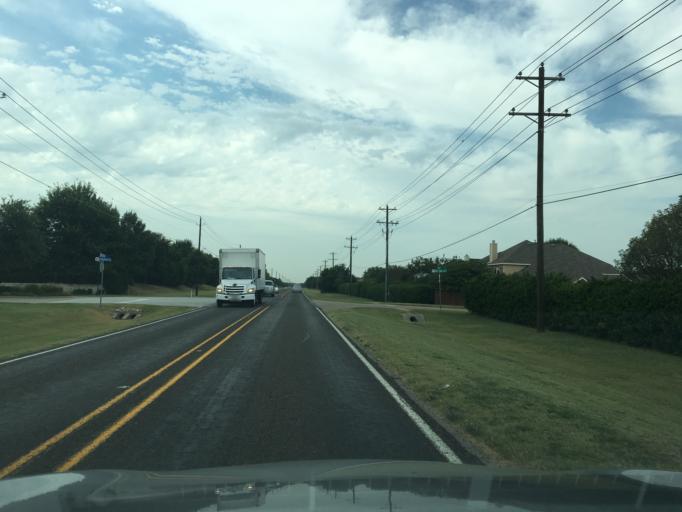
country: US
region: Texas
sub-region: Collin County
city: Parker
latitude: 33.0830
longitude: -96.6202
